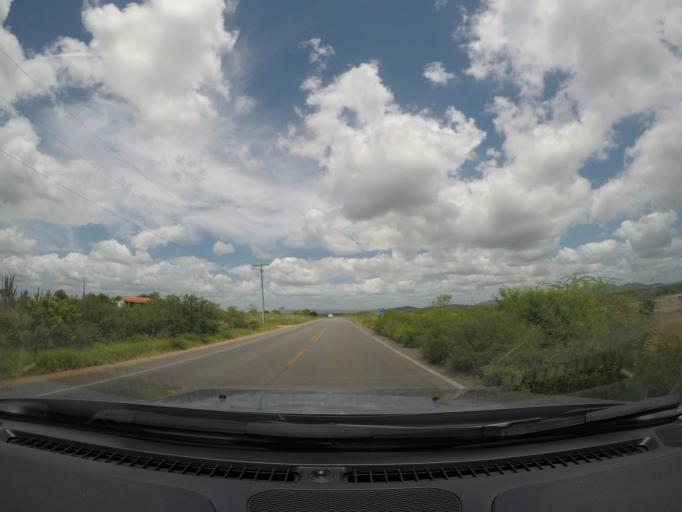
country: BR
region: Bahia
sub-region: Ipira
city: Ipira
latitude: -12.2952
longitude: -39.8853
